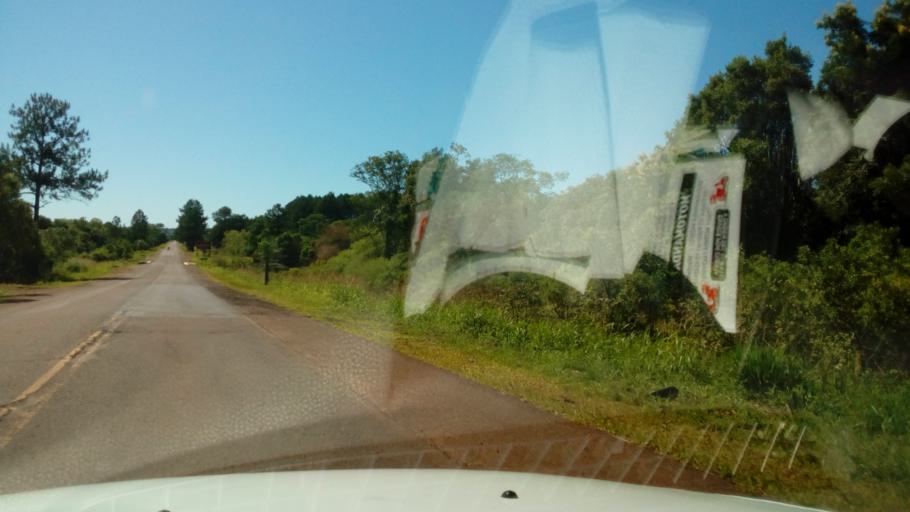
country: AR
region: Misiones
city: Almafuerte
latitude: -27.5657
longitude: -55.4030
